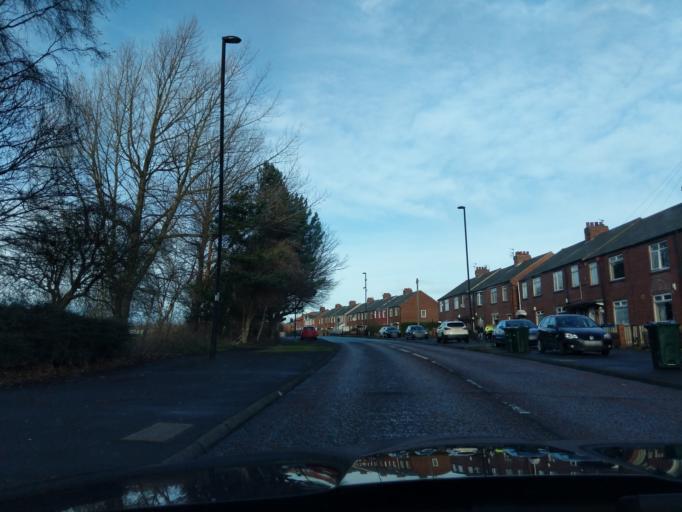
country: GB
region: England
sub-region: Gateshead
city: Felling
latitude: 54.9681
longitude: -1.5677
